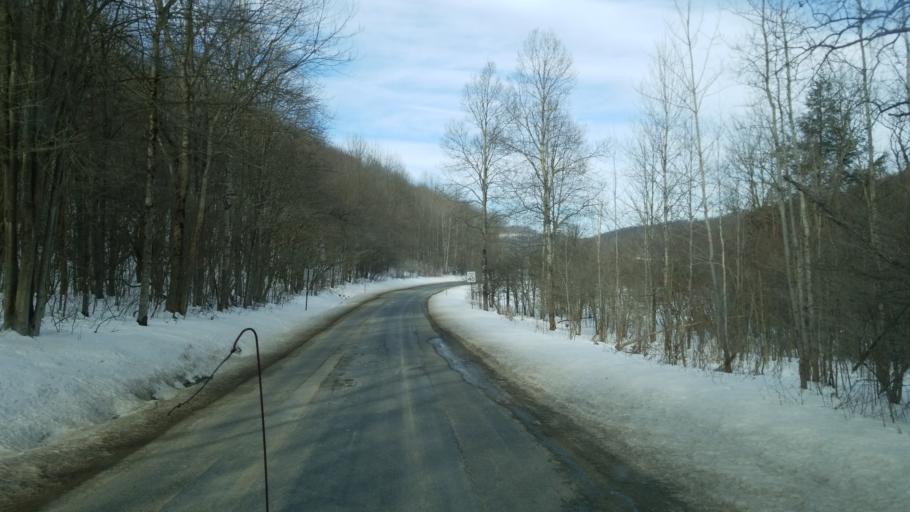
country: US
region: New York
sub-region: Allegany County
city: Andover
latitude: 41.9904
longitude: -77.7973
